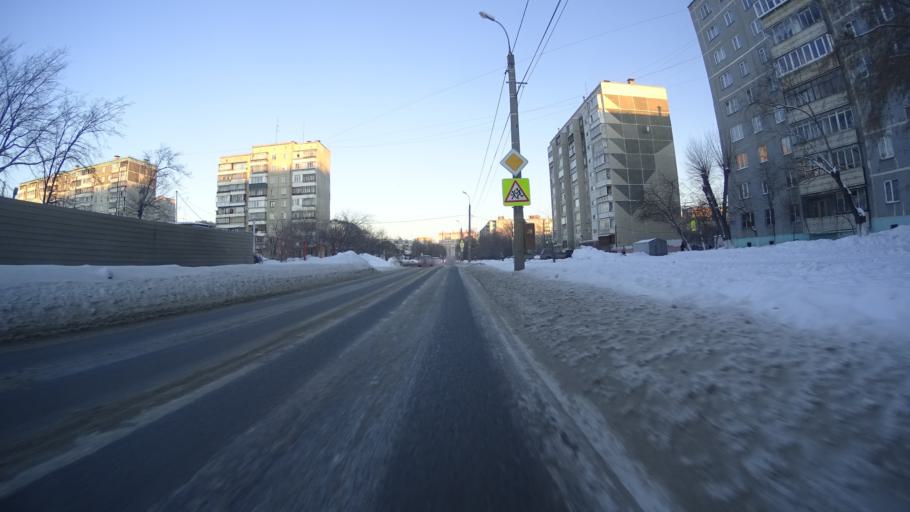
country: RU
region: Chelyabinsk
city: Roshchino
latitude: 55.1988
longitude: 61.3106
